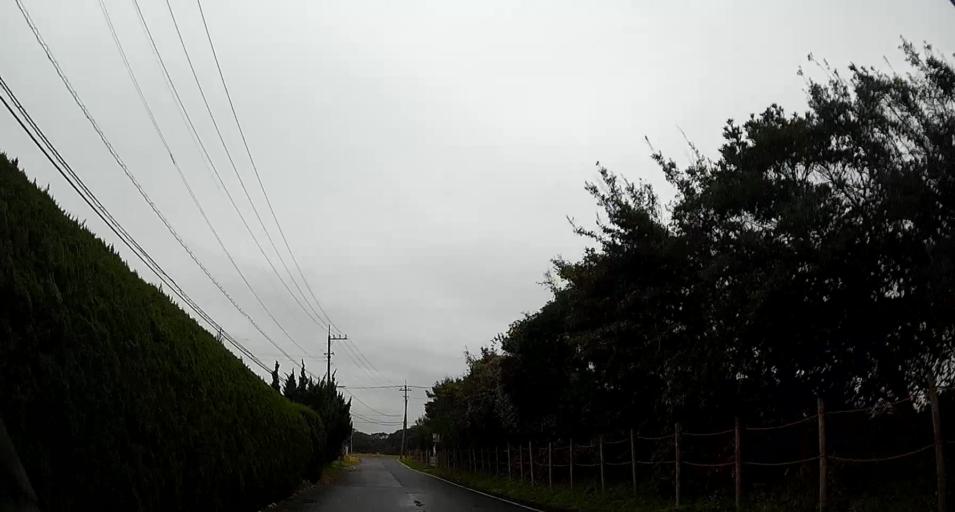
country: JP
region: Chiba
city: Kisarazu
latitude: 35.4210
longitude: 139.9009
